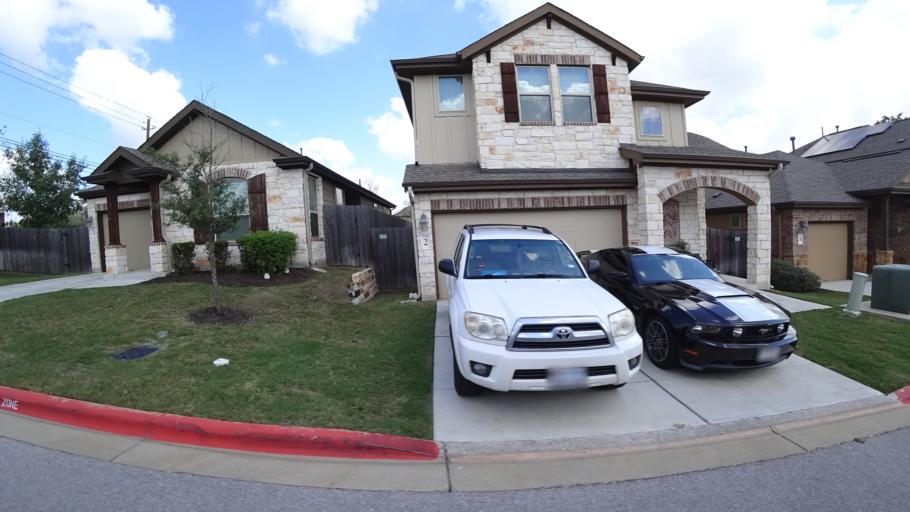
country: US
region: Texas
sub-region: Travis County
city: Manchaca
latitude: 30.1972
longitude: -97.8086
